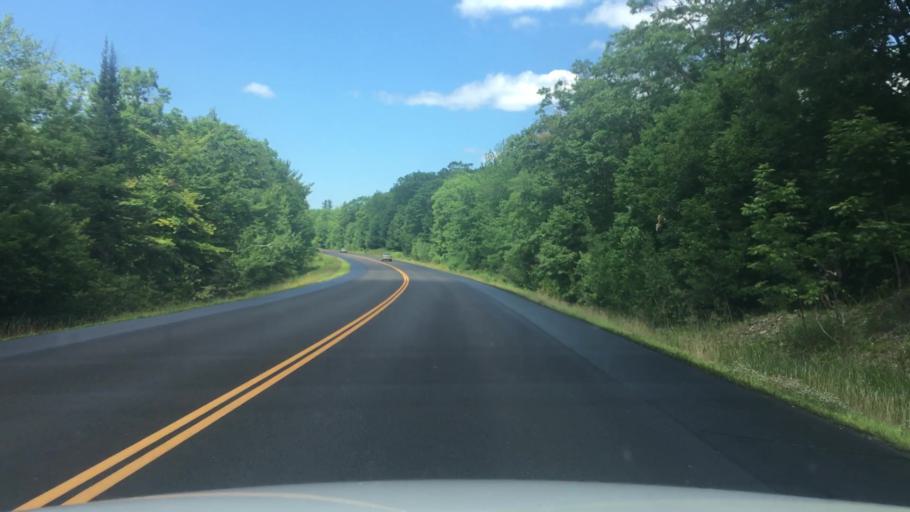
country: US
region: Maine
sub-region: Waldo County
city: Searsmont
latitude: 44.4099
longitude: -69.1771
